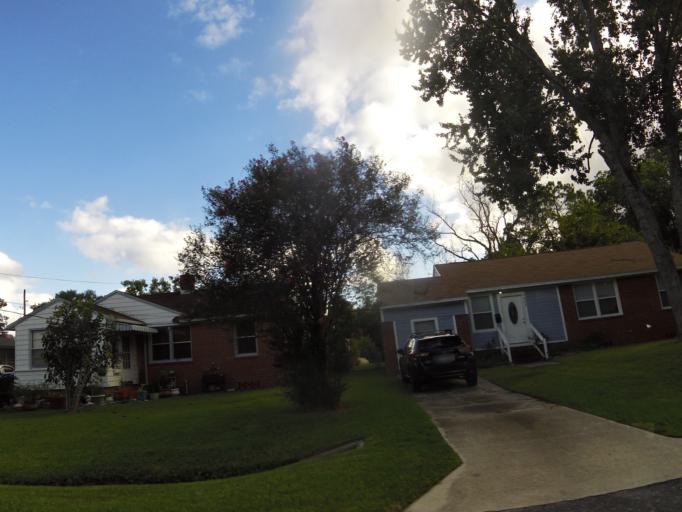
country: US
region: Florida
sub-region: Duval County
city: Jacksonville
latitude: 30.2869
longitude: -81.7257
